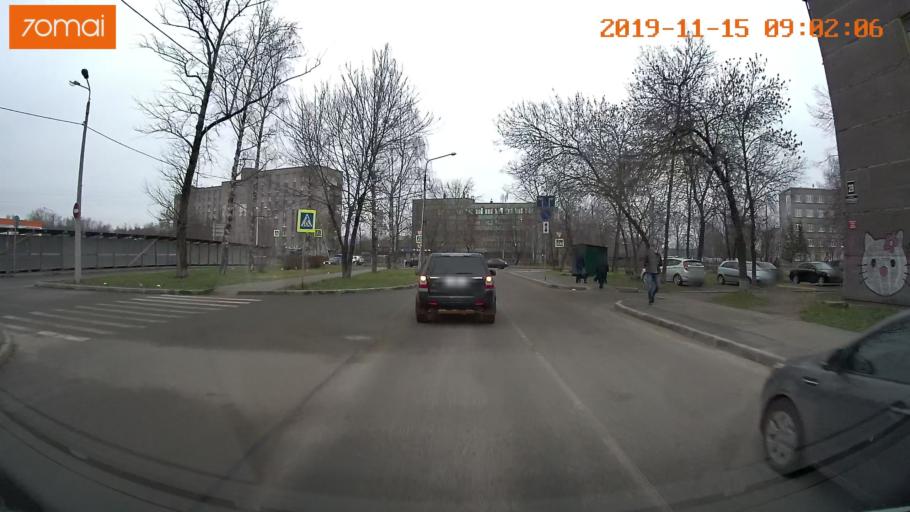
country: RU
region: Vologda
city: Cherepovets
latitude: 59.1357
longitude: 37.9269
